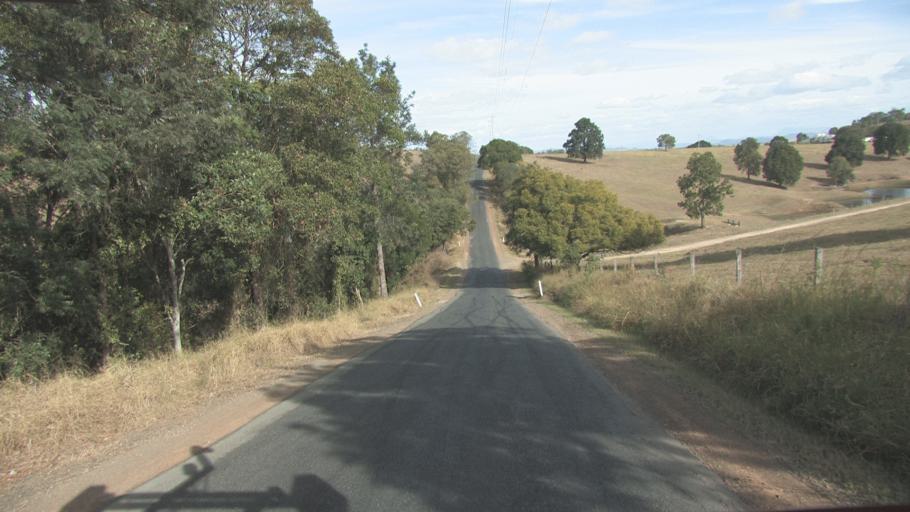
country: AU
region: Queensland
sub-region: Logan
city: Cedar Vale
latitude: -27.9018
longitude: 153.0151
